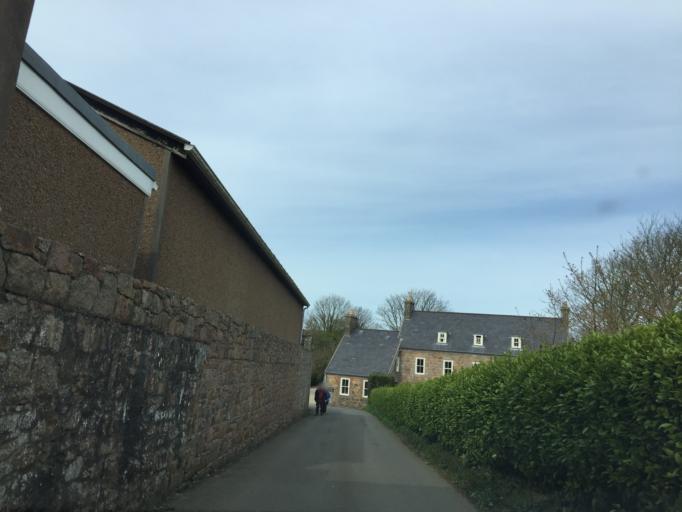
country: JE
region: St Helier
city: Saint Helier
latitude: 49.2494
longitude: -2.1677
